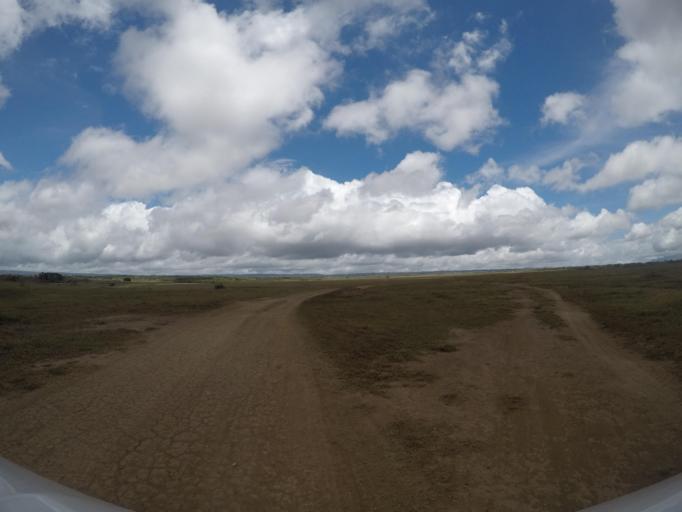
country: TL
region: Lautem
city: Lospalos
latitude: -8.4541
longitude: 126.9856
